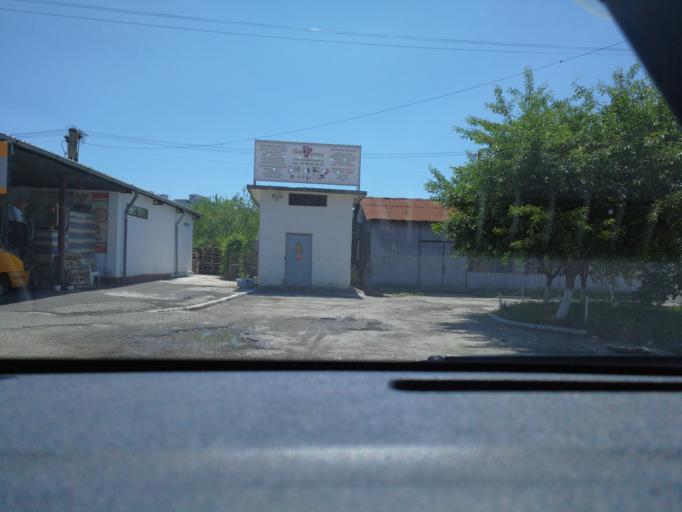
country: RO
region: Prahova
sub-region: Comuna Barcanesti
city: Tatarani
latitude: 44.9244
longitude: 26.0316
